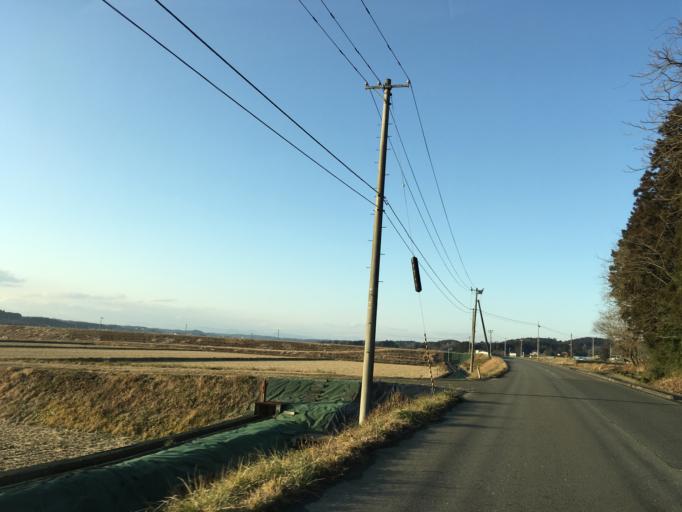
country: JP
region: Iwate
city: Ichinoseki
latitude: 38.8102
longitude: 141.2149
